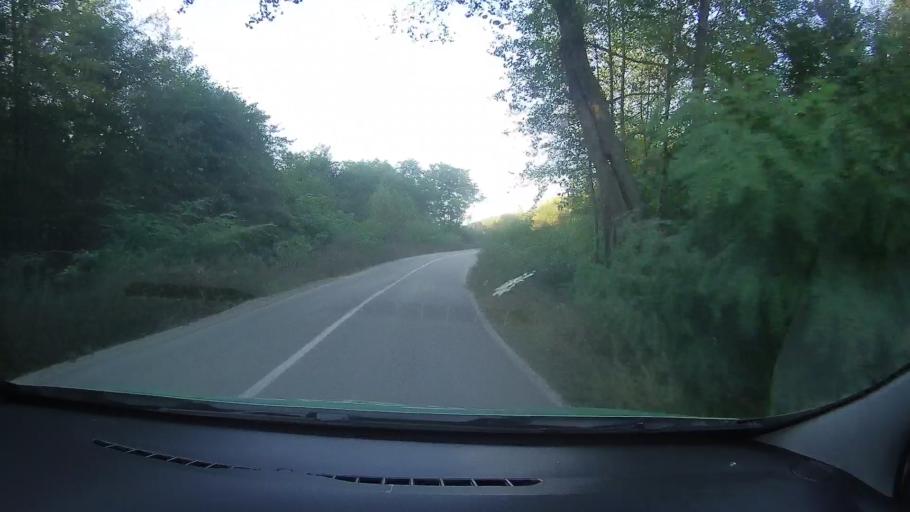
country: RO
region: Timis
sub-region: Comuna Fardea
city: Fardea
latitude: 45.6954
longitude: 22.1598
